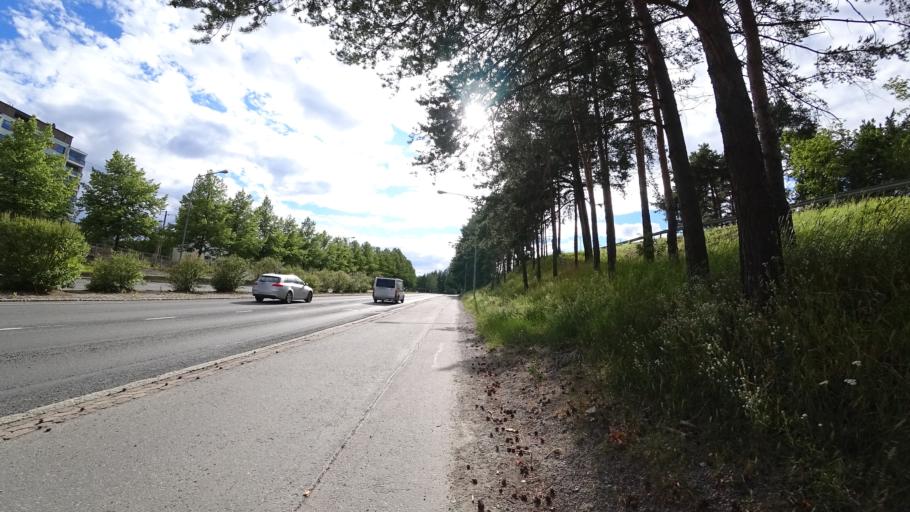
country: FI
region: Pirkanmaa
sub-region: Tampere
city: Tampere
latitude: 61.5027
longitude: 23.7424
